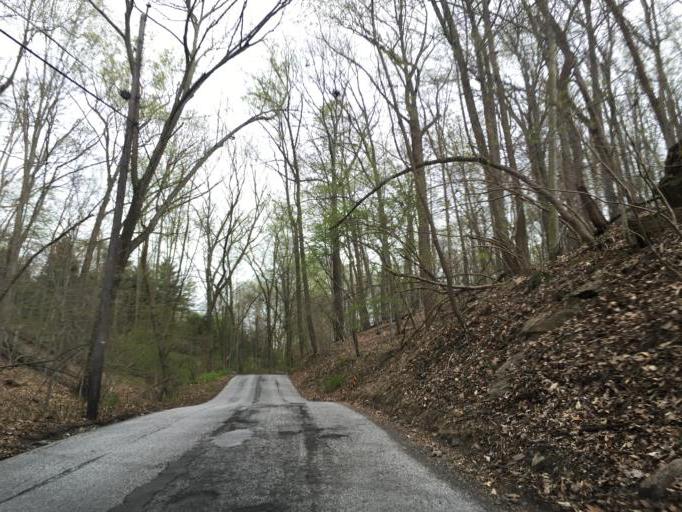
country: US
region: Maryland
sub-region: Baltimore County
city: Hunt Valley
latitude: 39.5032
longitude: -76.6128
